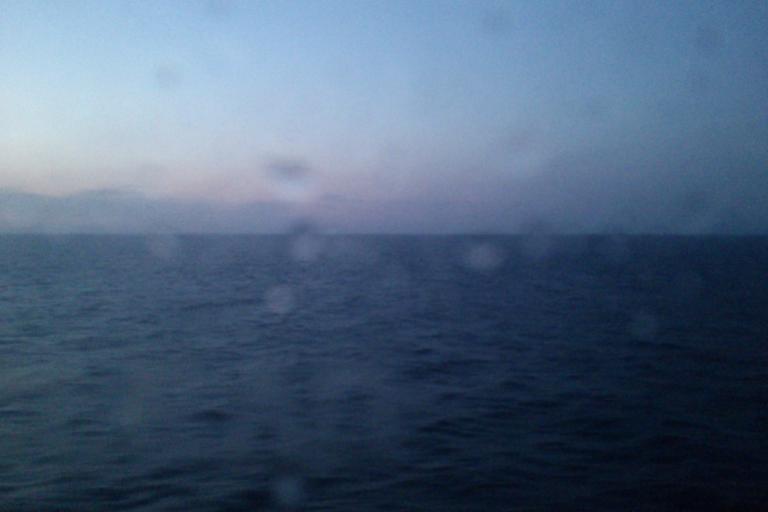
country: JP
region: Ishikawa
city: Kanazawa-shi
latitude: 37.0545
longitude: 136.0013
